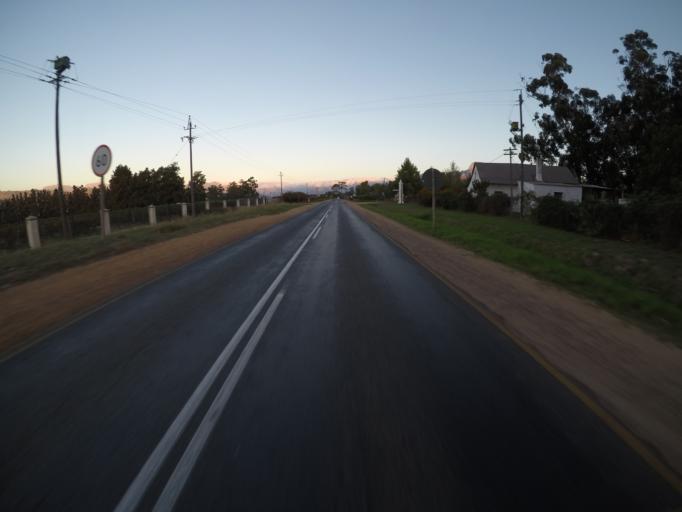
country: ZA
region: Western Cape
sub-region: Cape Winelands District Municipality
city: Paarl
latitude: -33.8338
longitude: 18.9502
